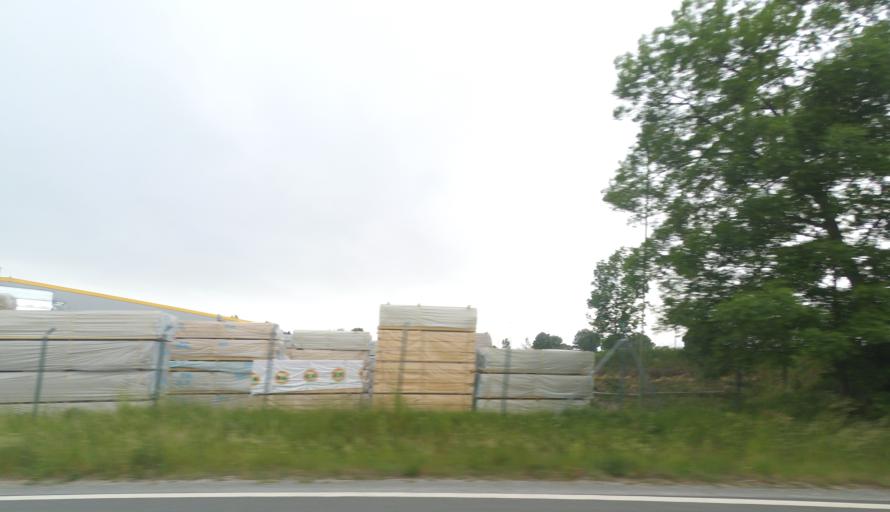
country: DE
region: Bavaria
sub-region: Upper Franconia
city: Weissenstadt
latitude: 50.1087
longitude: 11.8879
